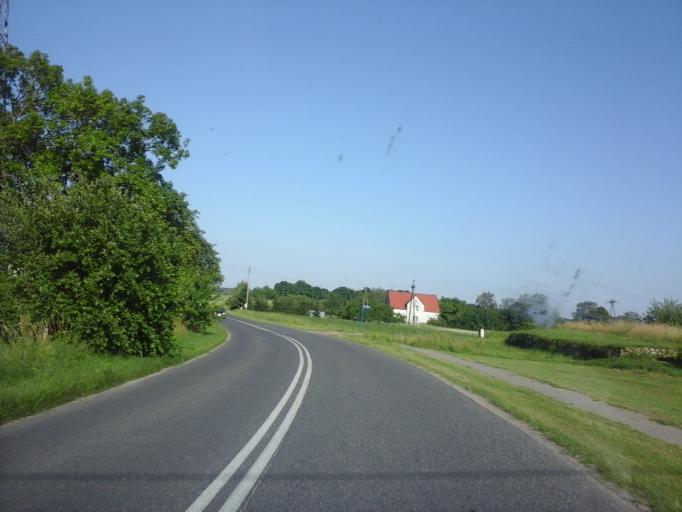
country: PL
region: West Pomeranian Voivodeship
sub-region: Powiat stargardzki
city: Chociwel
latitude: 53.4564
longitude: 15.3345
